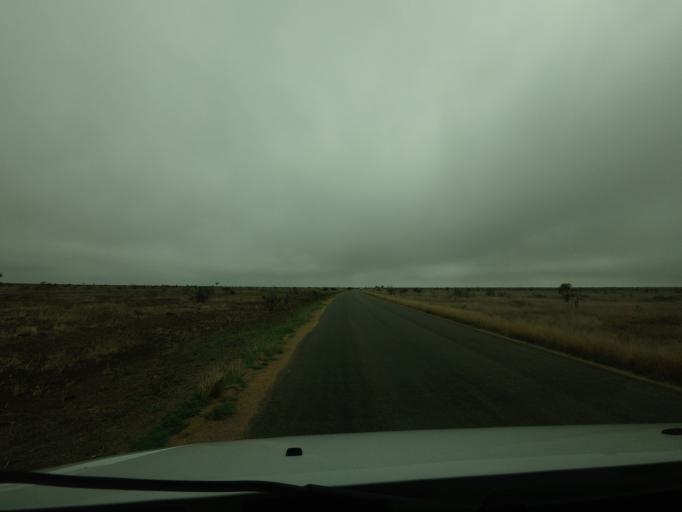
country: ZA
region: Limpopo
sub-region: Mopani District Municipality
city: Phalaborwa
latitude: -24.2354
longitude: 31.7199
